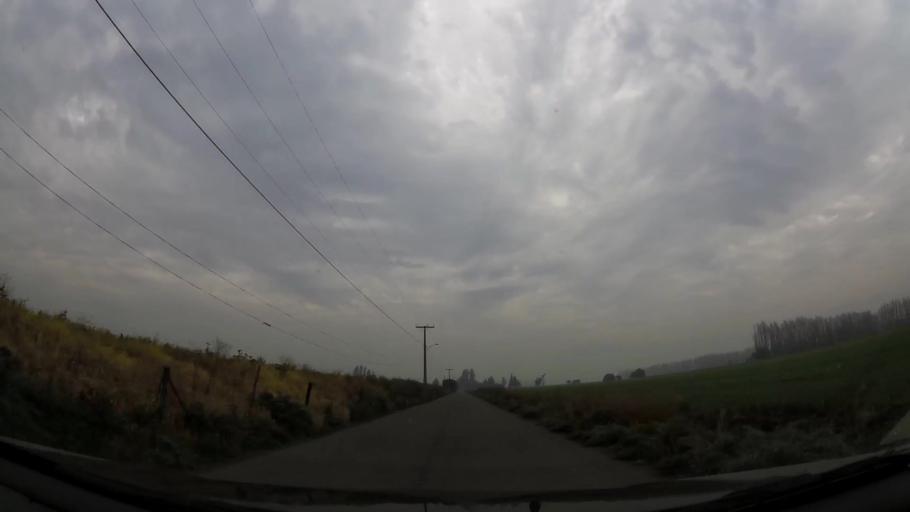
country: CL
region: Santiago Metropolitan
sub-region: Provincia de Chacabuco
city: Chicureo Abajo
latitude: -33.2607
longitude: -70.7629
